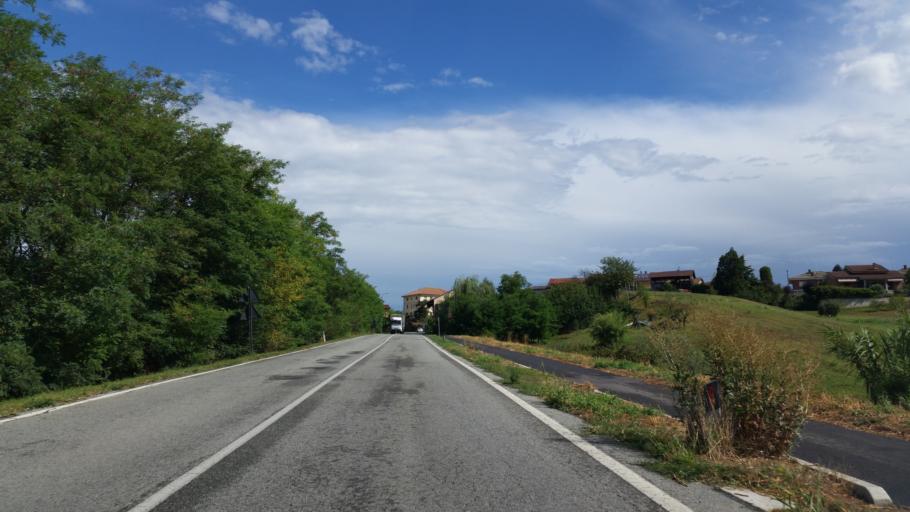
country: IT
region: Piedmont
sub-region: Provincia di Torino
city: Pralormo
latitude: 44.8664
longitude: 7.8964
